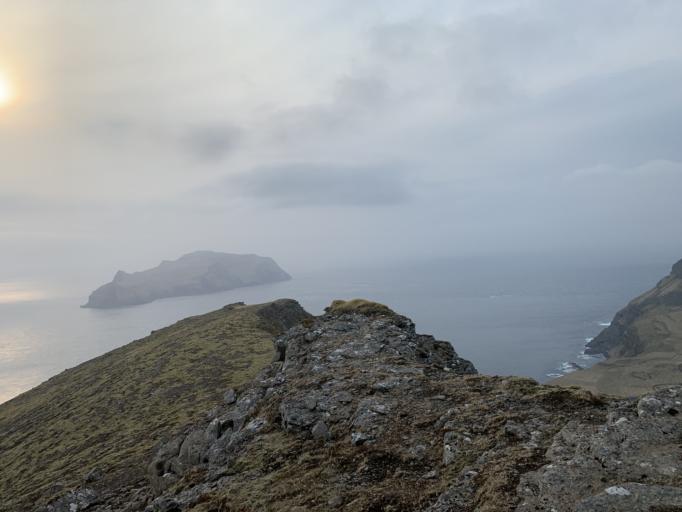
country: FO
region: Vagar
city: Sorvagur
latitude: 62.1027
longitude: -7.4227
